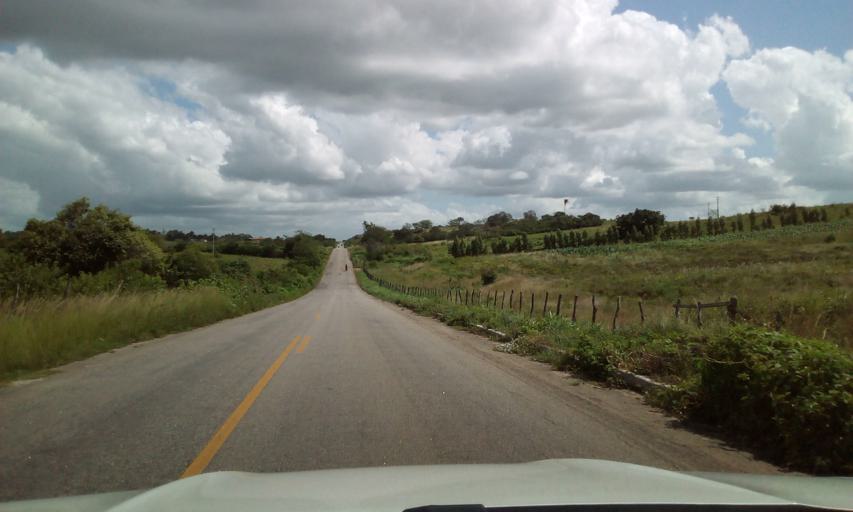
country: BR
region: Paraiba
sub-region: Guarabira
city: Guarabira
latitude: -6.8531
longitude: -35.4014
